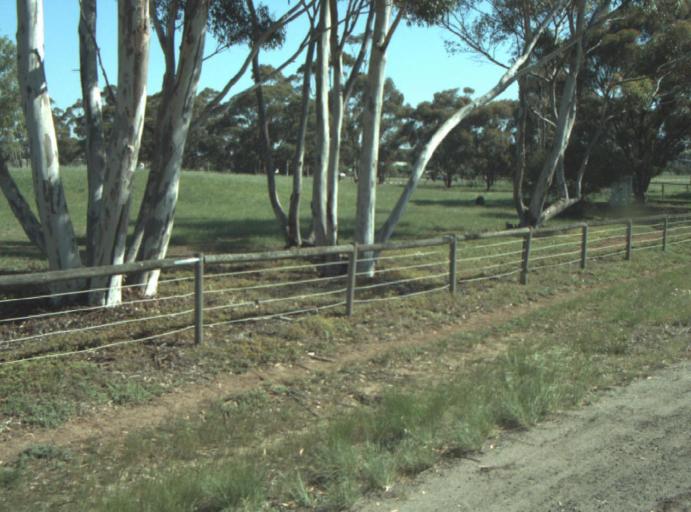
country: AU
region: Victoria
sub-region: Greater Geelong
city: Lara
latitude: -38.0291
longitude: 144.3557
